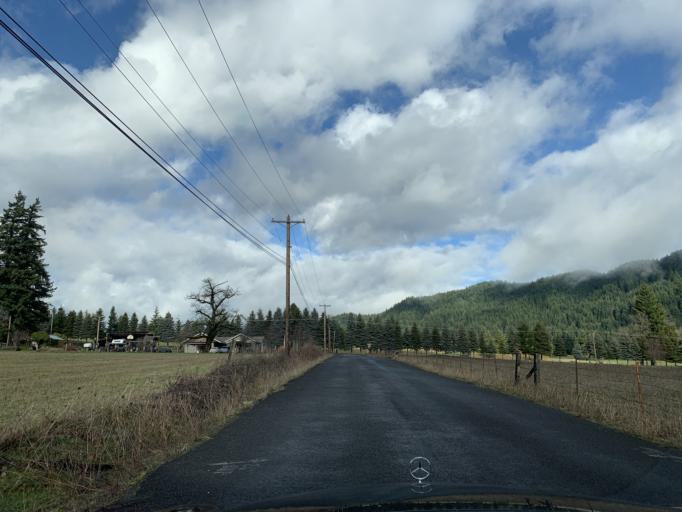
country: US
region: Washington
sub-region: Skamania County
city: Carson
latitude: 45.7245
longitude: -121.8048
